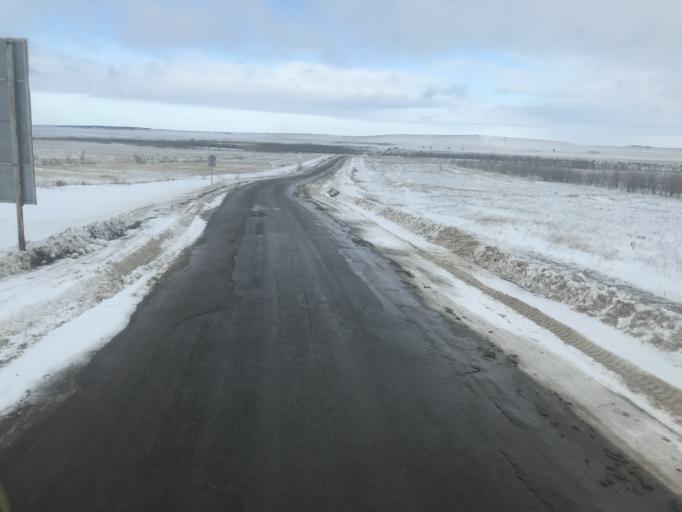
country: RU
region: Saratov
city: Staryye Ozinki
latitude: 51.2180
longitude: 49.8780
